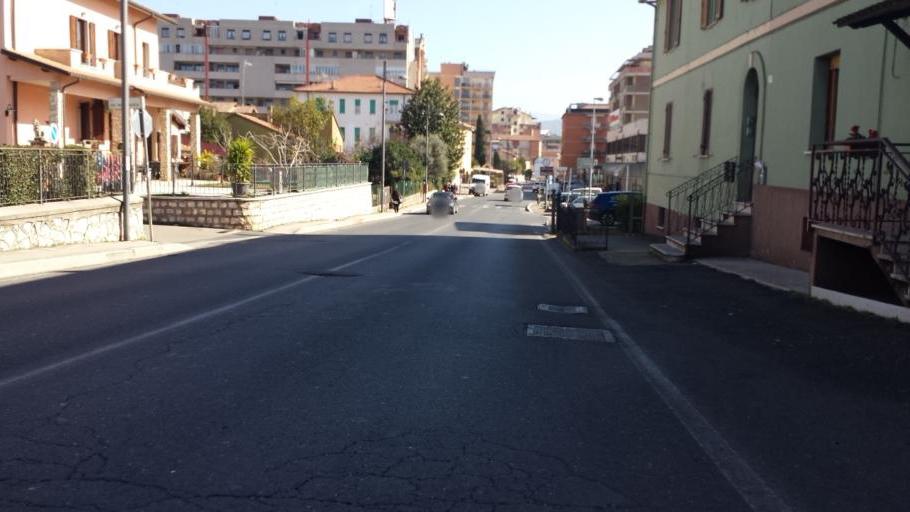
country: IT
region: Umbria
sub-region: Provincia di Terni
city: Terni
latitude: 42.5814
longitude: 12.6200
